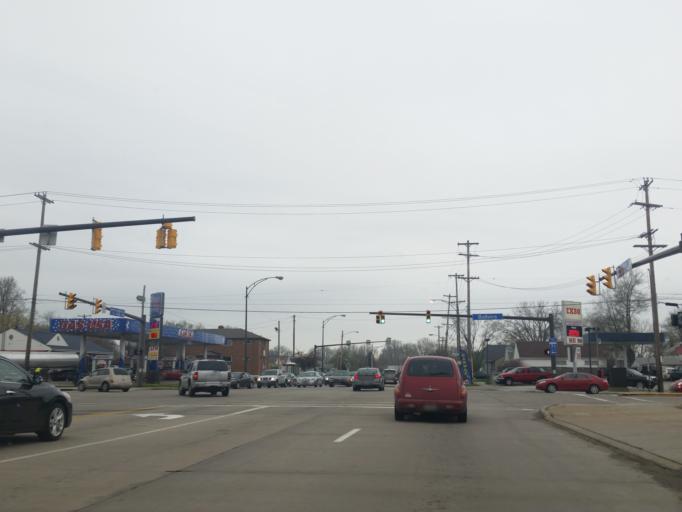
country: US
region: Ohio
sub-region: Cuyahoga County
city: Brooklyn
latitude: 41.4464
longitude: -81.7664
